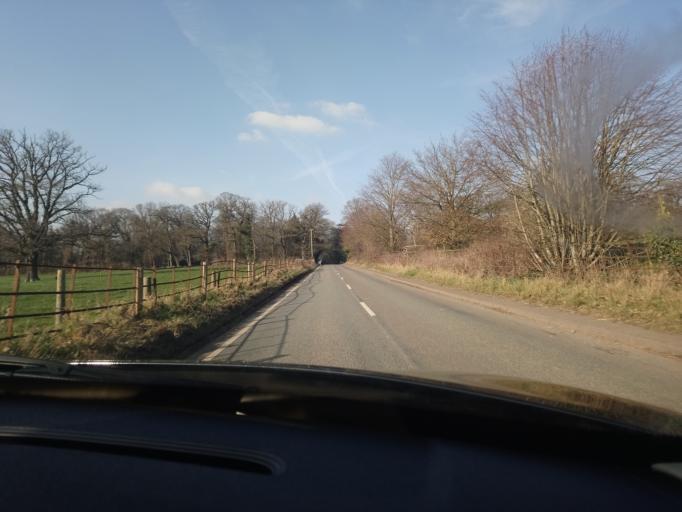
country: GB
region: England
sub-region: Shropshire
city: Shrewsbury
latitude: 52.7332
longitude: -2.7761
